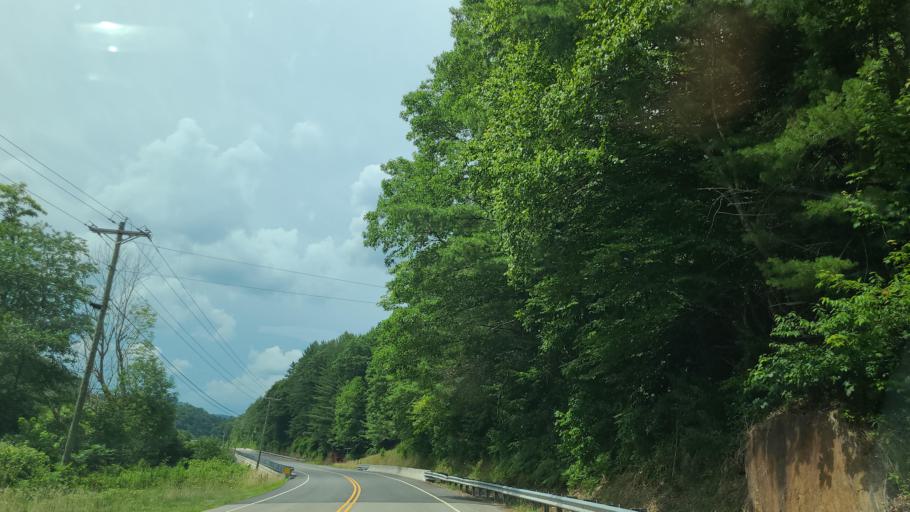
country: US
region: North Carolina
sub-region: Ashe County
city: Jefferson
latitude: 36.3839
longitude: -81.4003
